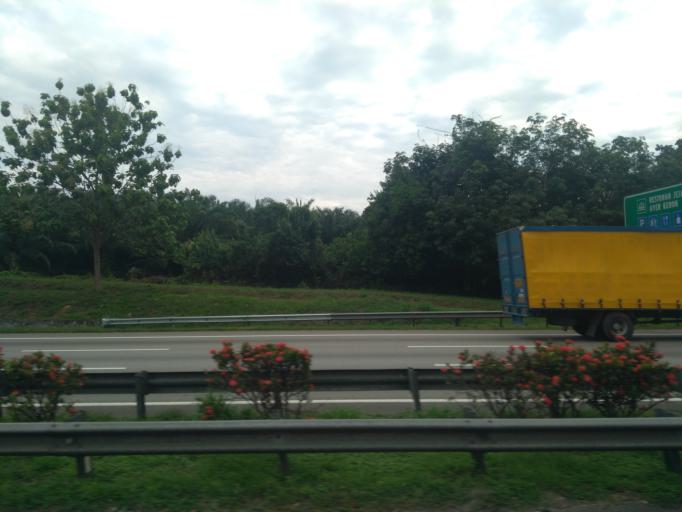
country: MY
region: Melaka
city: Alor Gajah
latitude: 2.3899
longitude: 102.2261
